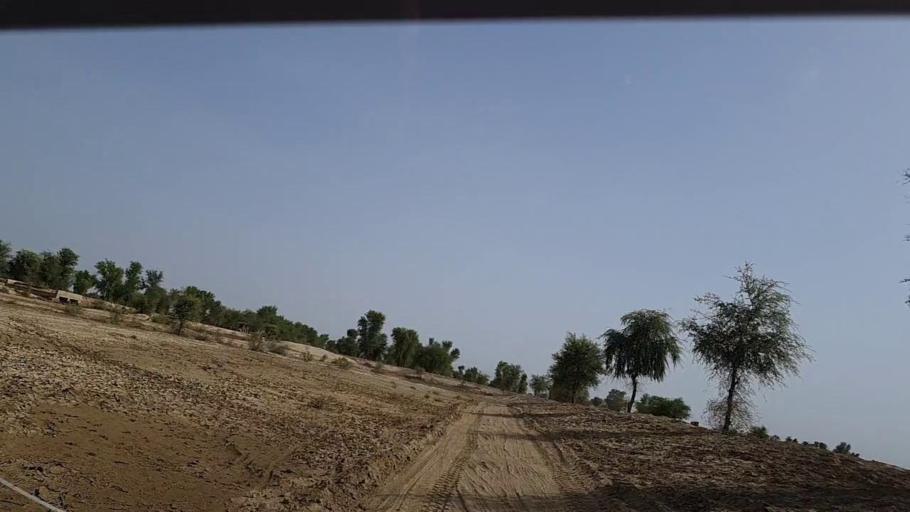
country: PK
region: Sindh
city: Johi
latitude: 26.6392
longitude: 67.5024
